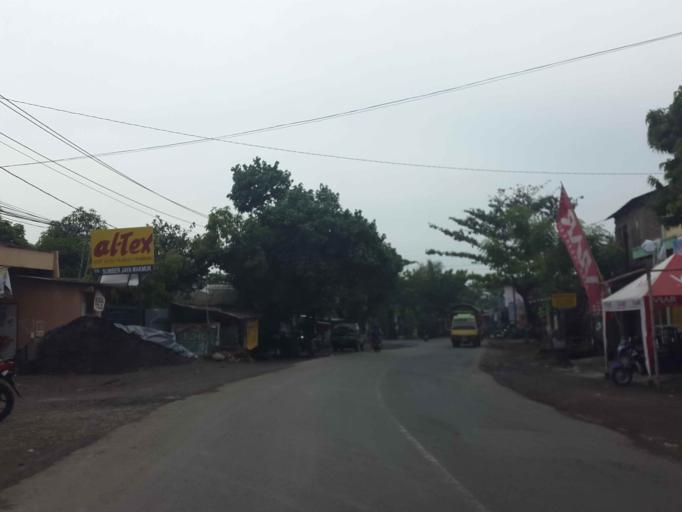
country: ID
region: Central Java
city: Mranggen
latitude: -6.9738
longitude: 110.4816
